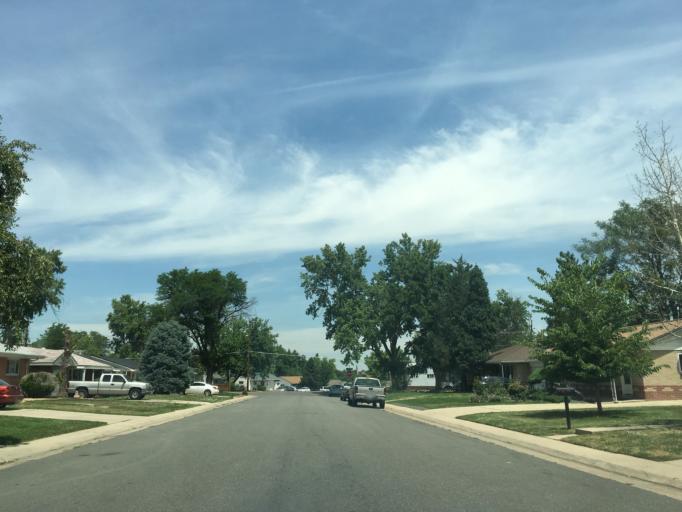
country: US
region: Colorado
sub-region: Arapahoe County
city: Sheridan
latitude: 39.6814
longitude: -105.0403
